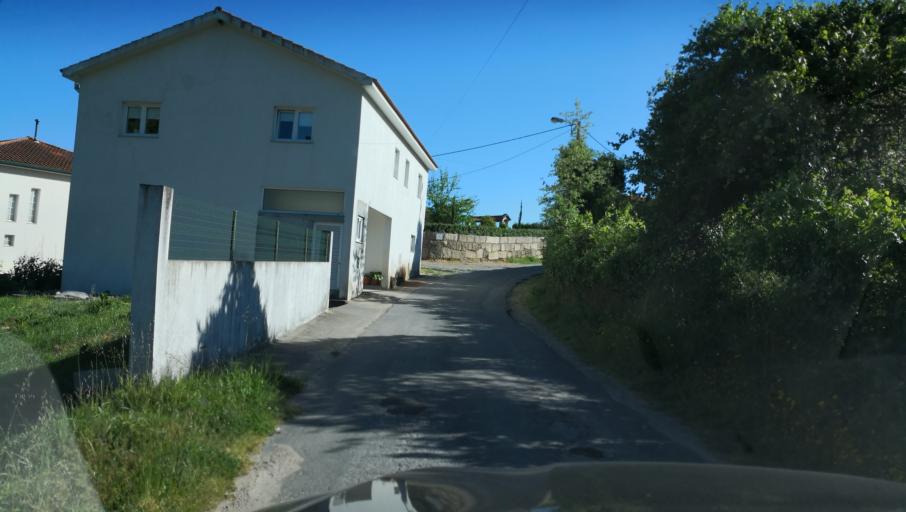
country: PT
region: Vila Real
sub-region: Vila Real
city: Vila Real
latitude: 41.3373
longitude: -7.7385
